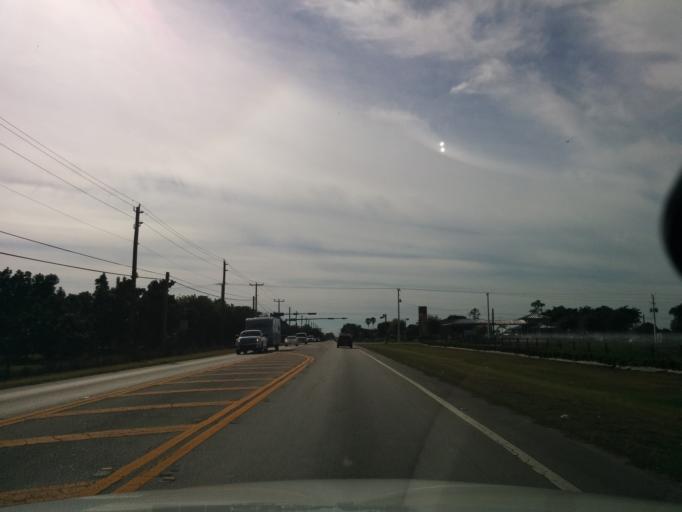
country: US
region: Florida
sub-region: Miami-Dade County
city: Naranja
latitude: 25.5278
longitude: -80.4779
